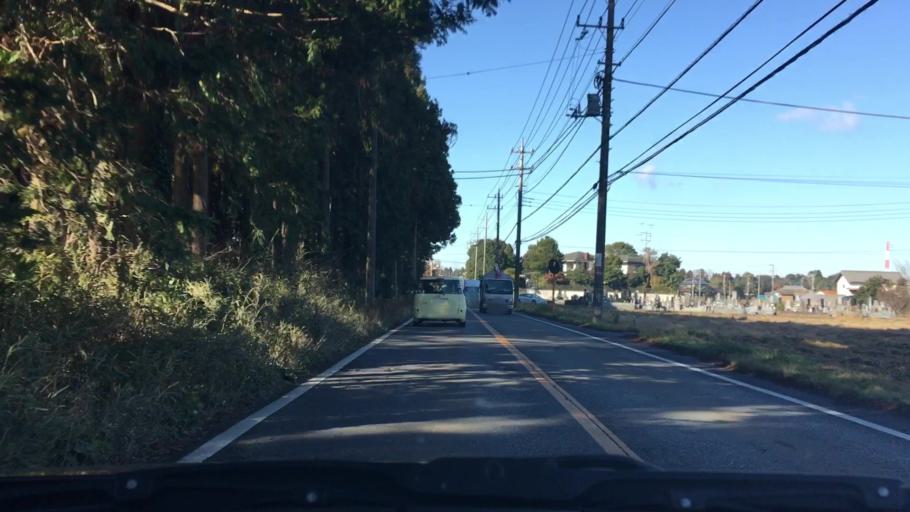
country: JP
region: Chiba
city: Sawara
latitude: 35.7980
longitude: 140.4491
